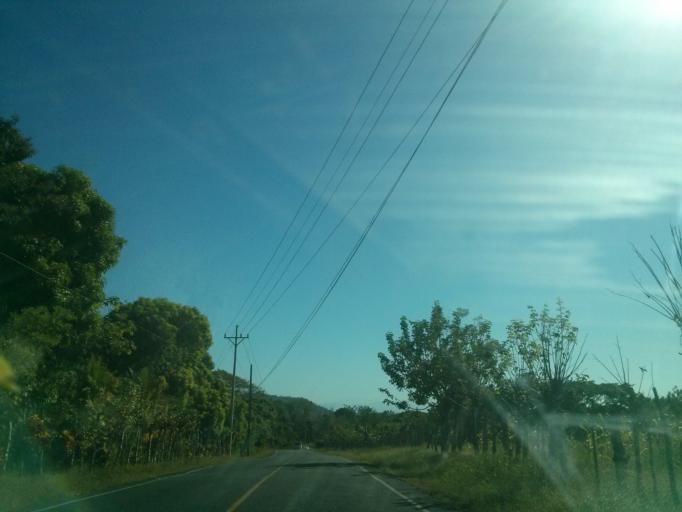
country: CR
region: Puntarenas
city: Paquera
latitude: 9.7027
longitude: -85.0400
